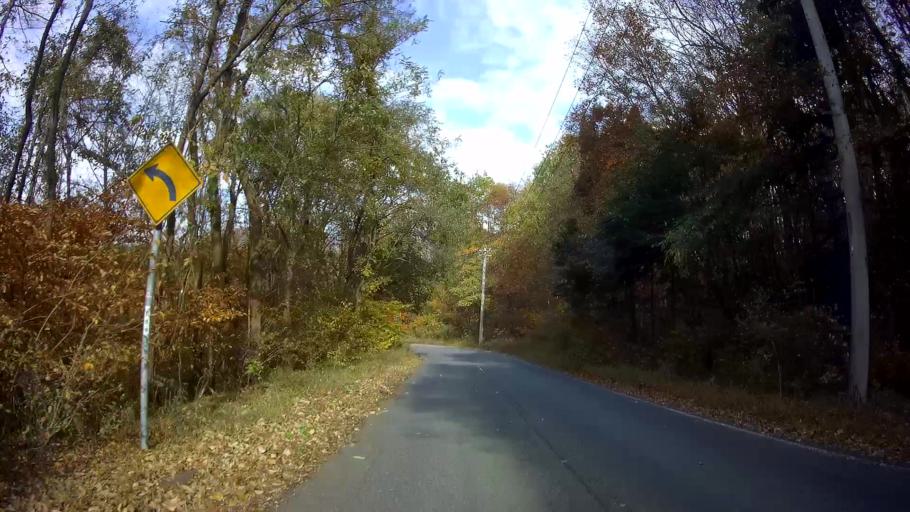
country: JP
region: Gunma
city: Nakanojomachi
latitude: 36.5324
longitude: 138.6596
